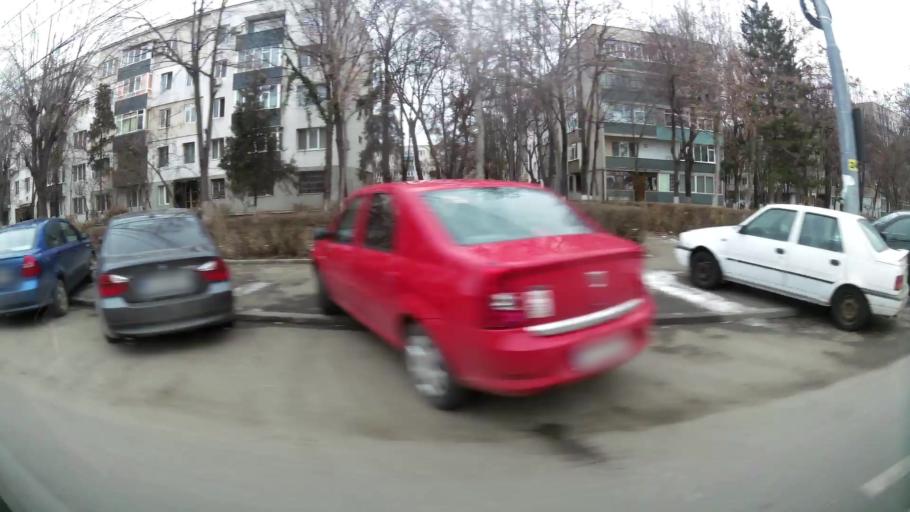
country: RO
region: Prahova
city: Ploiesti
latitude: 44.9305
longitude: 26.0320
